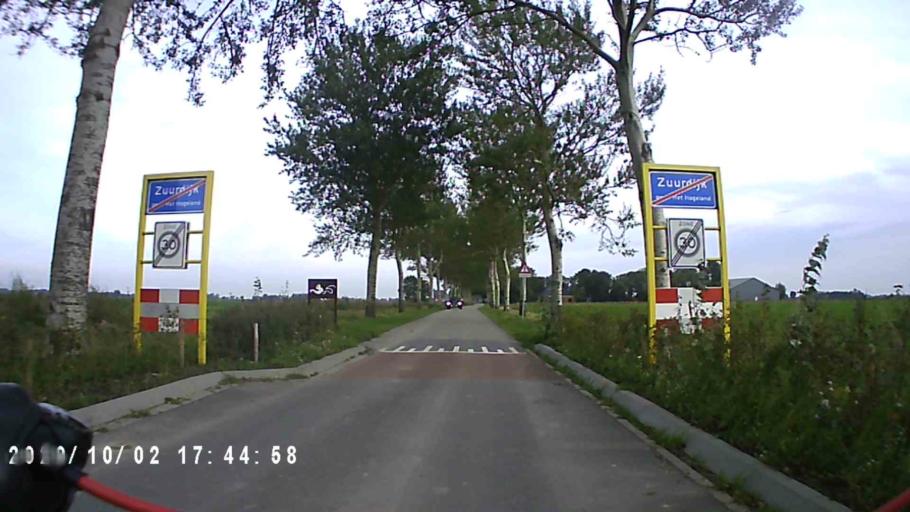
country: NL
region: Groningen
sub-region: Gemeente Zuidhorn
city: Oldehove
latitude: 53.3345
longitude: 6.3895
